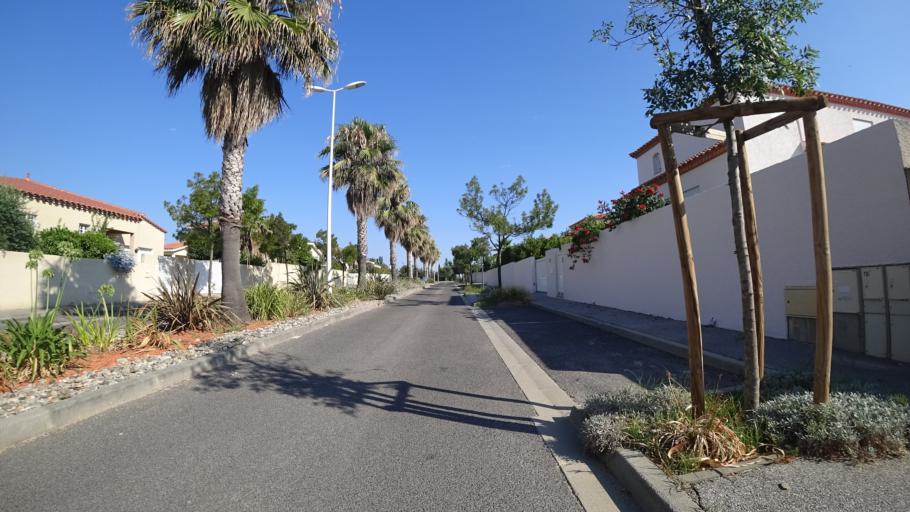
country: FR
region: Languedoc-Roussillon
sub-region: Departement des Pyrenees-Orientales
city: Cabestany
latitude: 42.7002
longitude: 2.9309
